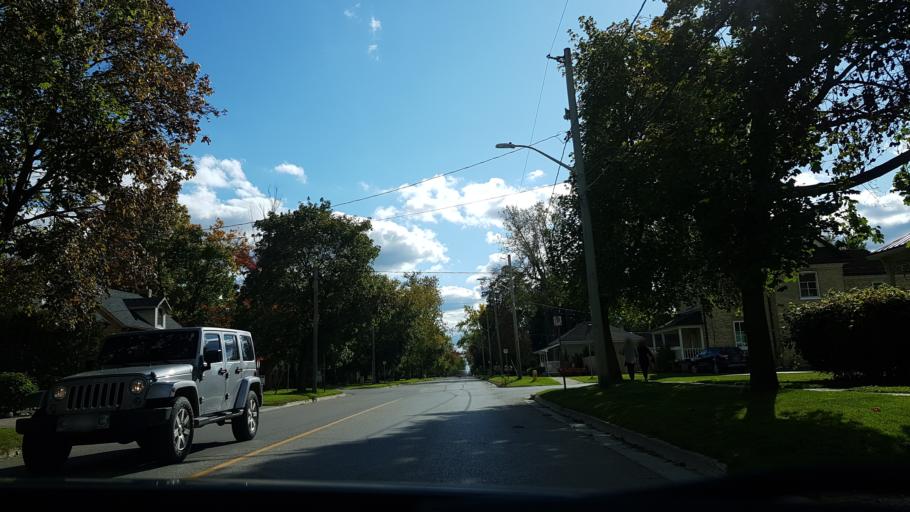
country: CA
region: Ontario
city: South Huron
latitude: 43.1606
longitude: -81.6847
